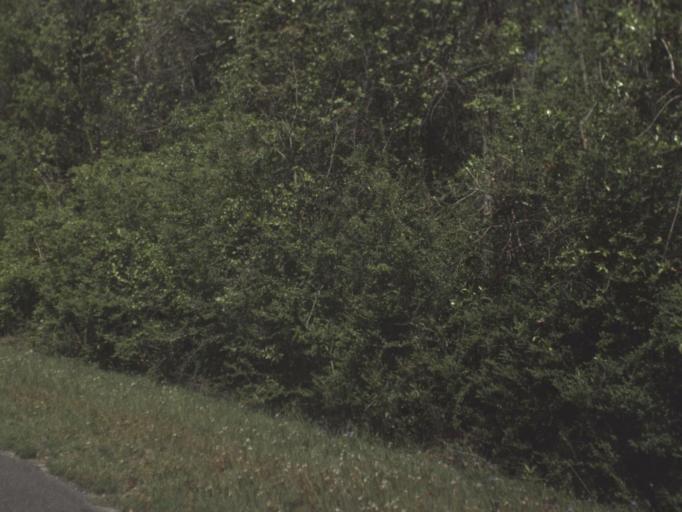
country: US
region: Florida
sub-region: Escambia County
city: Myrtle Grove
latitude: 30.4210
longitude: -87.3254
